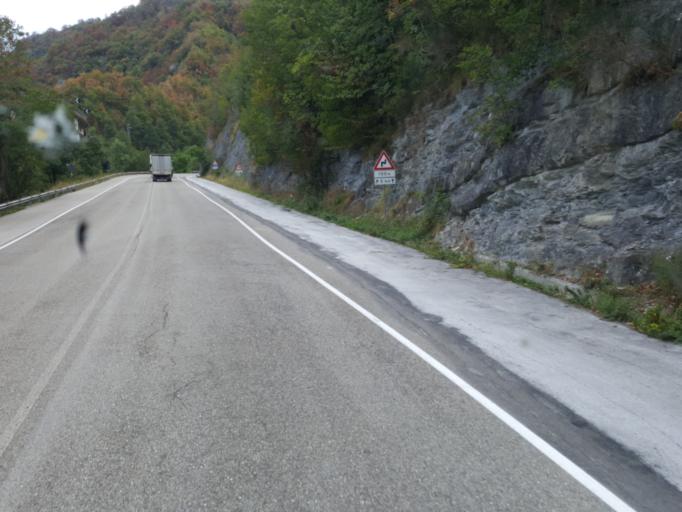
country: IT
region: Emilia-Romagna
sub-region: Forli-Cesena
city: San Piero in Bagno
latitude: 43.8234
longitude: 11.9574
